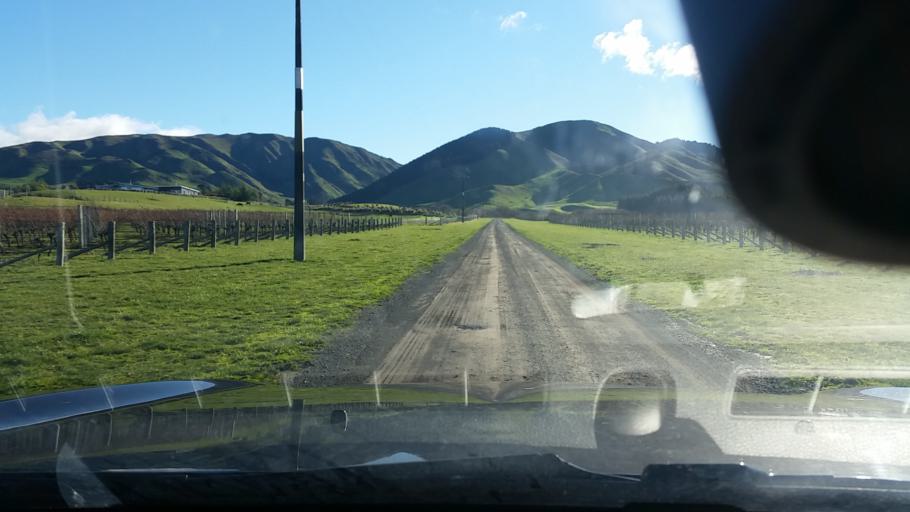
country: NZ
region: Marlborough
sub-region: Marlborough District
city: Blenheim
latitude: -41.6400
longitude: 174.0362
